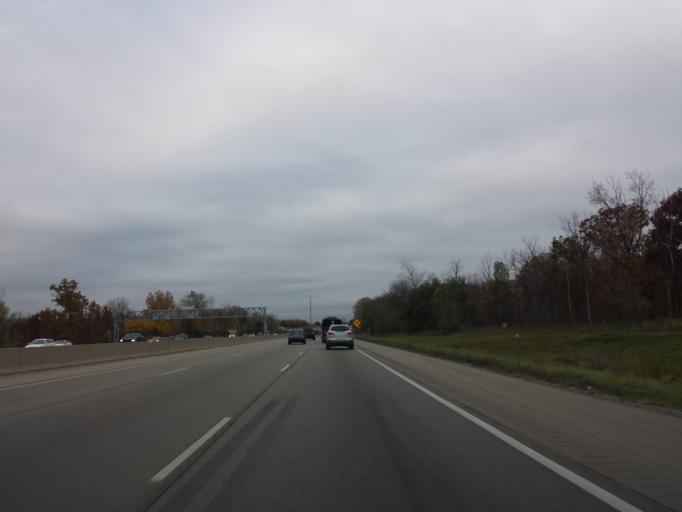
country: US
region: Michigan
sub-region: Oakland County
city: Auburn Hills
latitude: 42.6430
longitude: -83.2235
